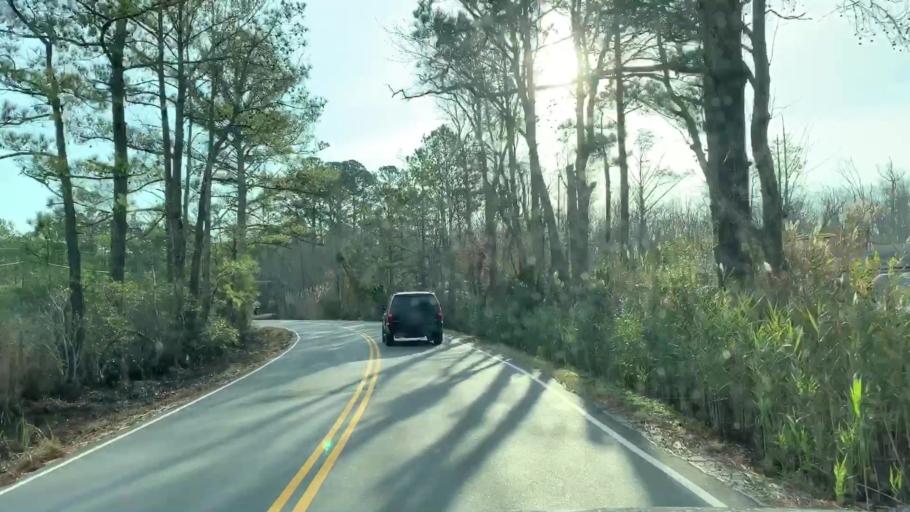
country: US
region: Virginia
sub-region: City of Virginia Beach
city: Virginia Beach
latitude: 36.6920
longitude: -76.0362
